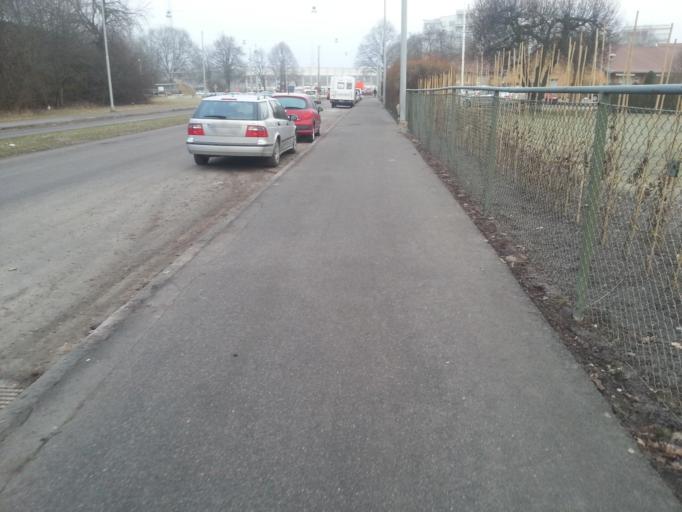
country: SE
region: OEstergoetland
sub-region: Norrkopings Kommun
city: Norrkoping
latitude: 58.5819
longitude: 16.1775
